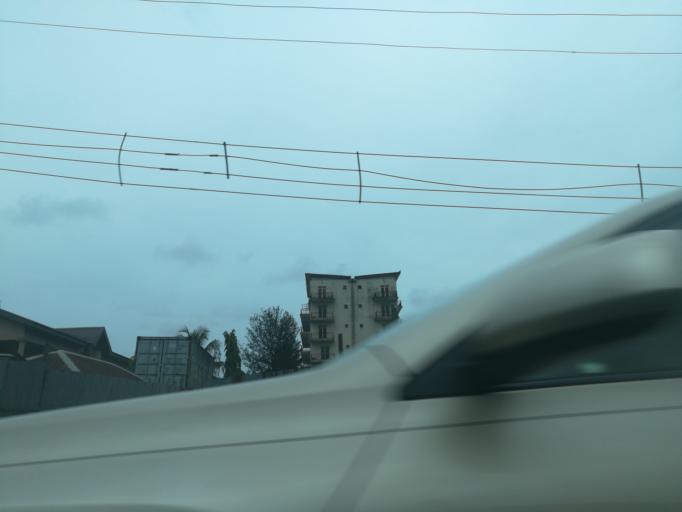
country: NG
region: Rivers
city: Port Harcourt
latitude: 4.8167
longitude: 6.9981
